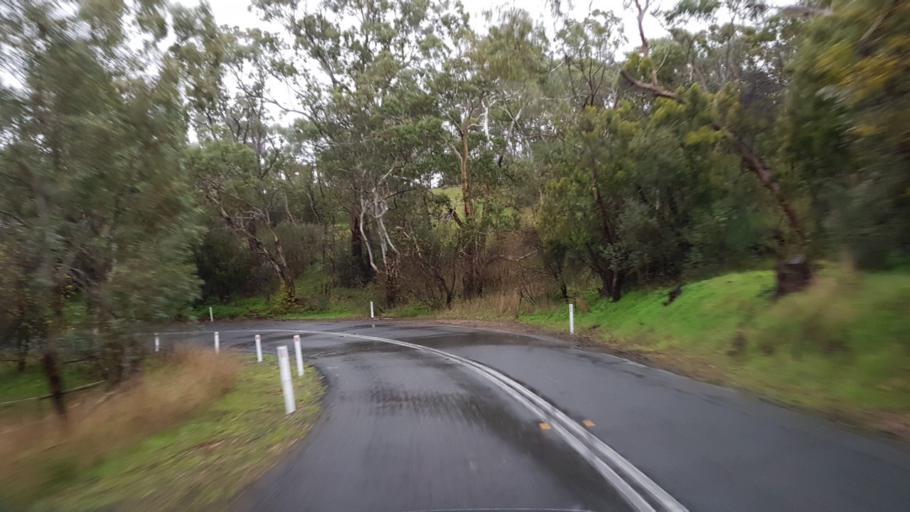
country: AU
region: South Australia
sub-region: Onkaparinga
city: Craigburn Farm
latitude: -35.0683
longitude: 138.6267
